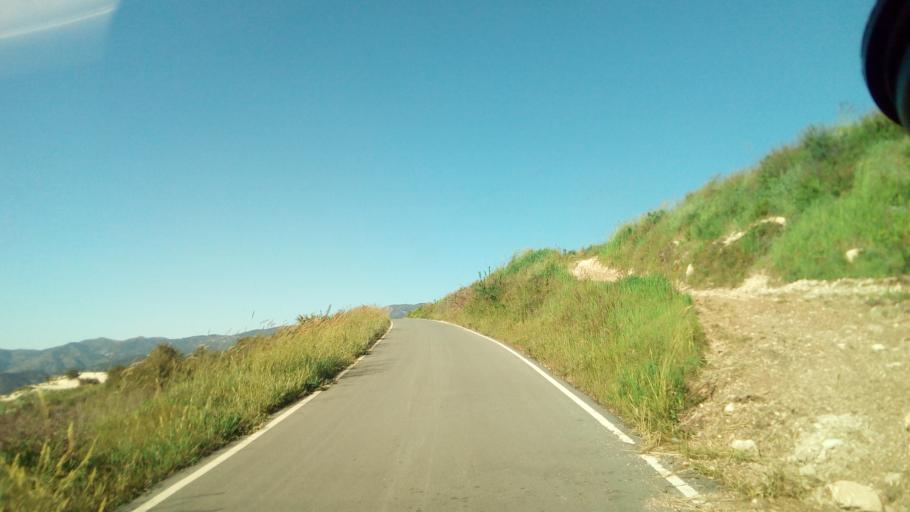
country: CY
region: Limassol
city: Pachna
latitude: 34.8634
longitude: 32.7704
